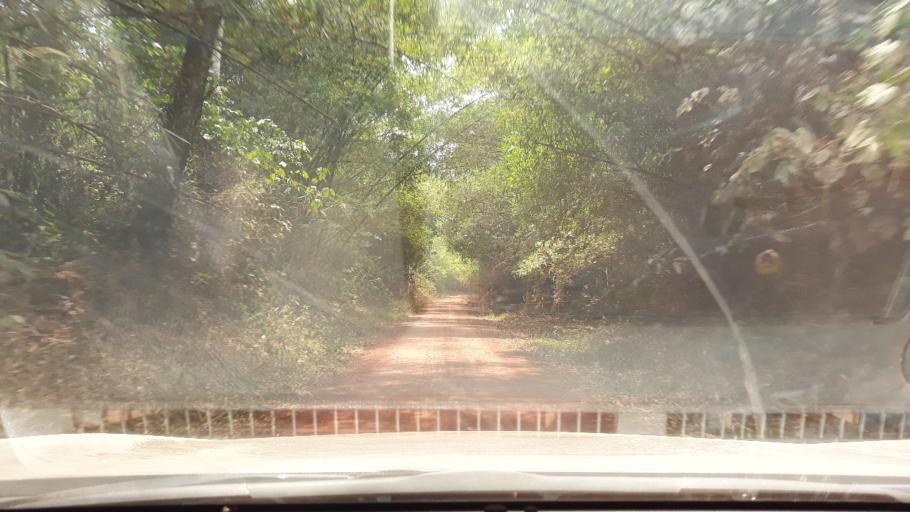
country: CD
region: Eastern Province
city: Buta
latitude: 2.3021
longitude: 25.0321
